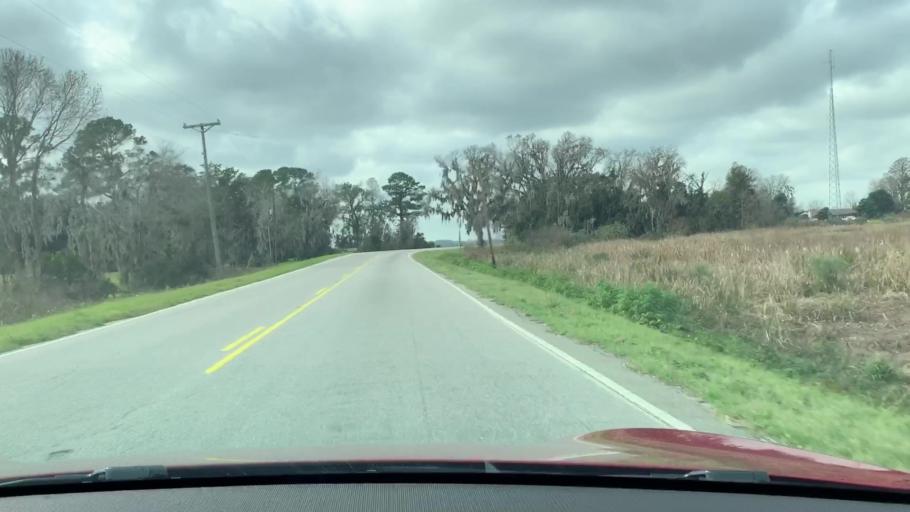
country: US
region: Georgia
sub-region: Chatham County
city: Port Wentworth
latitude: 32.1666
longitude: -81.1141
